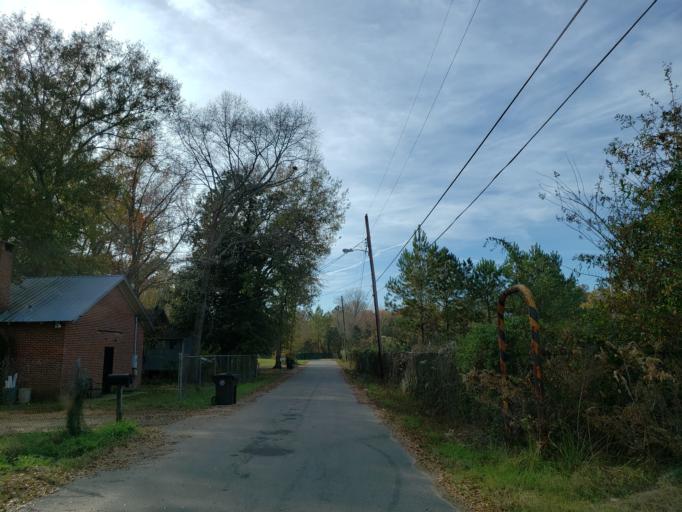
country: US
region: Mississippi
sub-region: Forrest County
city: Hattiesburg
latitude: 31.3345
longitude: -89.3077
